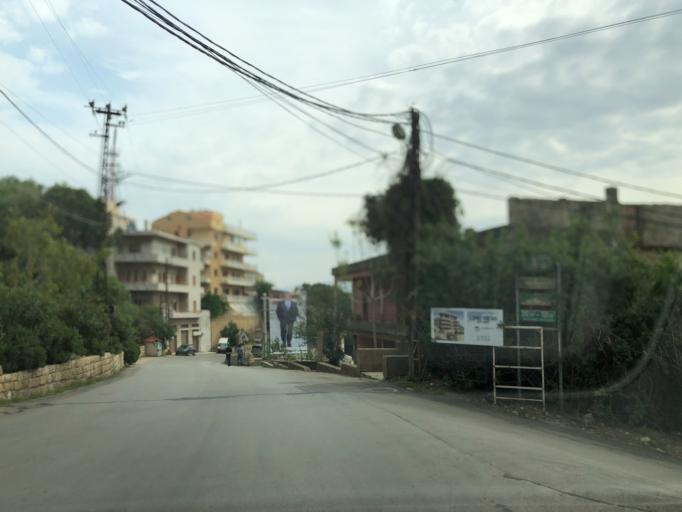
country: LB
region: Mont-Liban
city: Jdaidet el Matn
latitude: 33.8696
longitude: 35.6084
